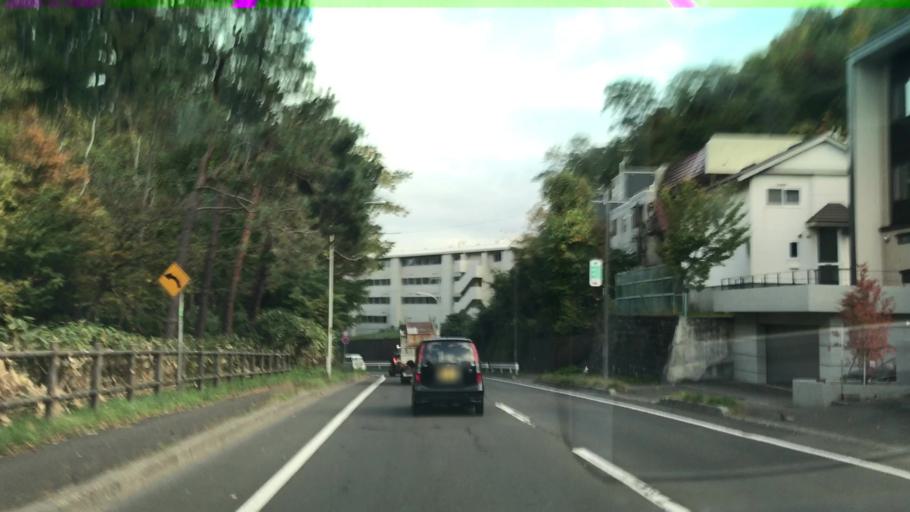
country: JP
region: Hokkaido
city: Sapporo
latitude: 43.0500
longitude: 141.2999
